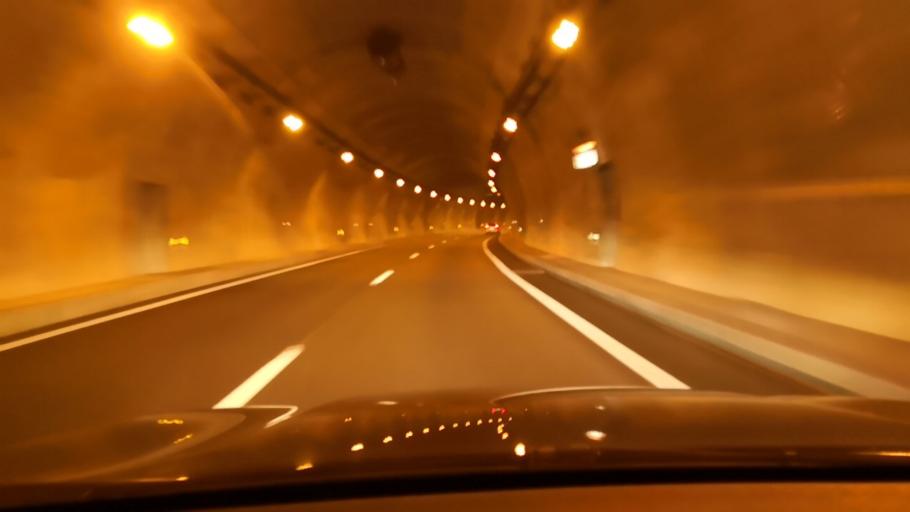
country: PT
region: Viseu
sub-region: Lamego
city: Lamego
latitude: 41.1218
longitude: -7.7790
